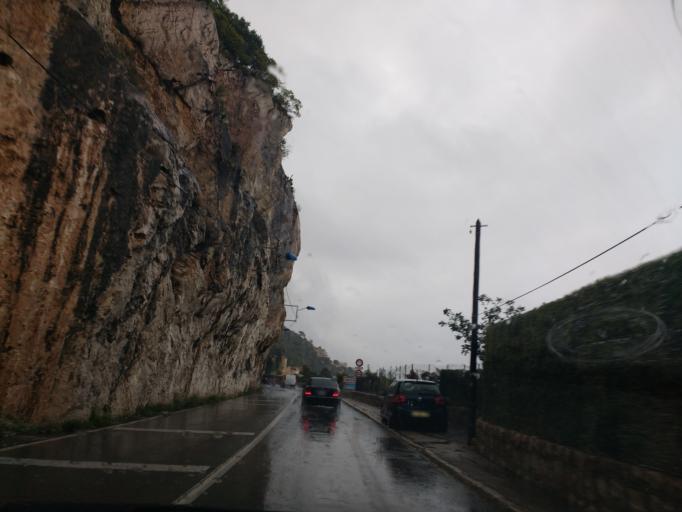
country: FR
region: Provence-Alpes-Cote d'Azur
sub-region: Departement des Alpes-Maritimes
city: Eze
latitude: 43.7232
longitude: 7.3831
